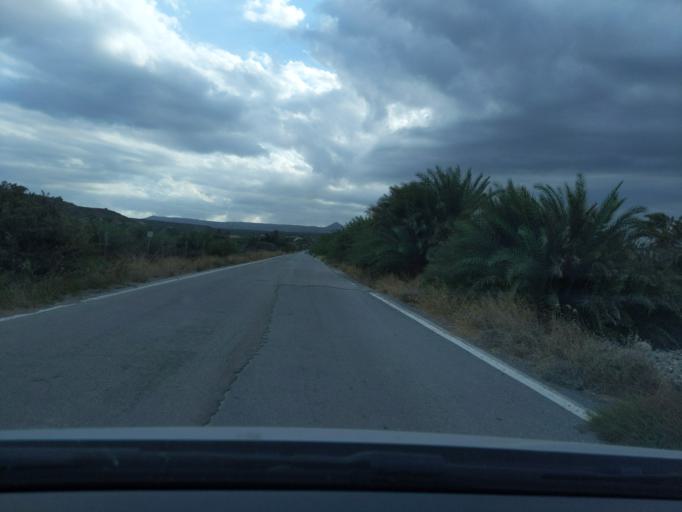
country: GR
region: Crete
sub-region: Nomos Lasithiou
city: Palekastro
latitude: 35.2594
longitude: 26.2560
